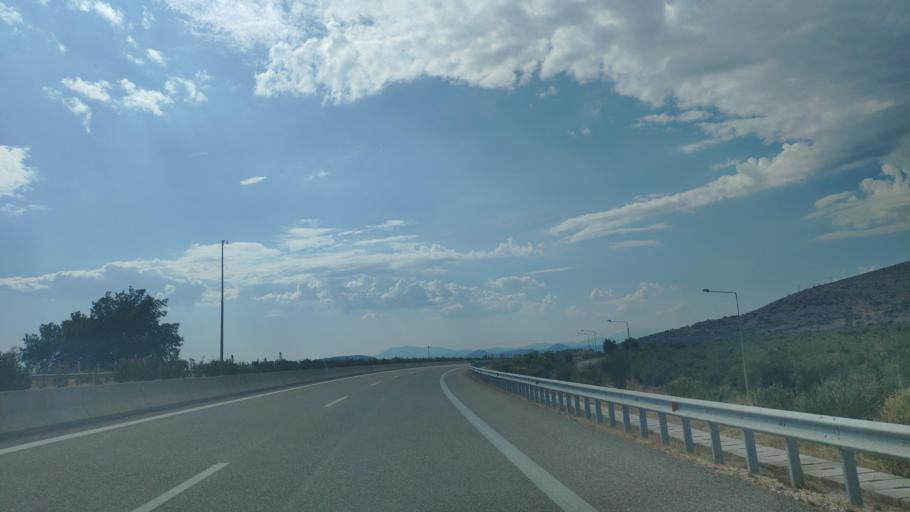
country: GR
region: West Greece
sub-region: Nomos Aitolias kai Akarnanias
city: Mesolongi
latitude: 38.4016
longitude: 21.4081
